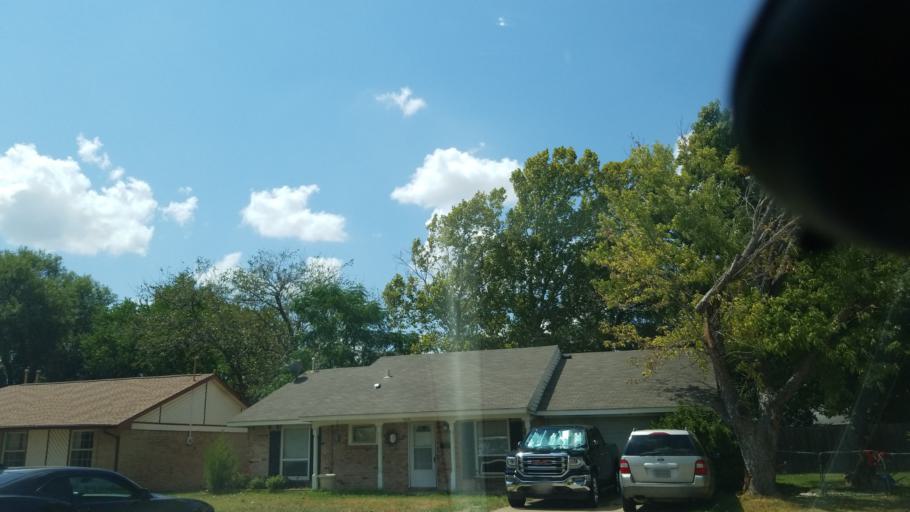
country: US
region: Texas
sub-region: Dallas County
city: Grand Prairie
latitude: 32.7233
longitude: -96.9967
